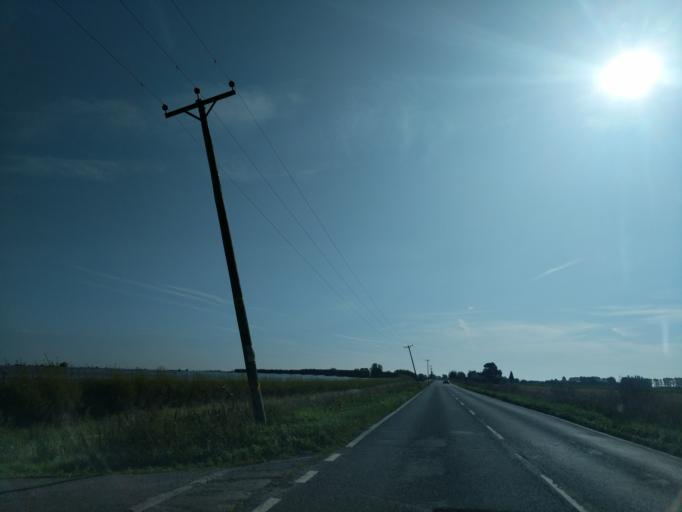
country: GB
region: England
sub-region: Lincolnshire
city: Bourne
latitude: 52.7721
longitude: -0.3229
